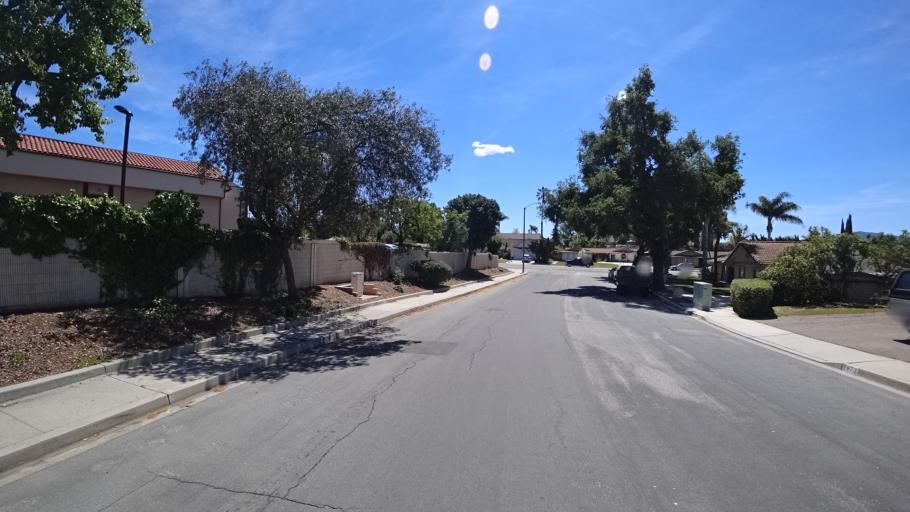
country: US
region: California
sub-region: Ventura County
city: Thousand Oaks
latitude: 34.2182
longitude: -118.8709
